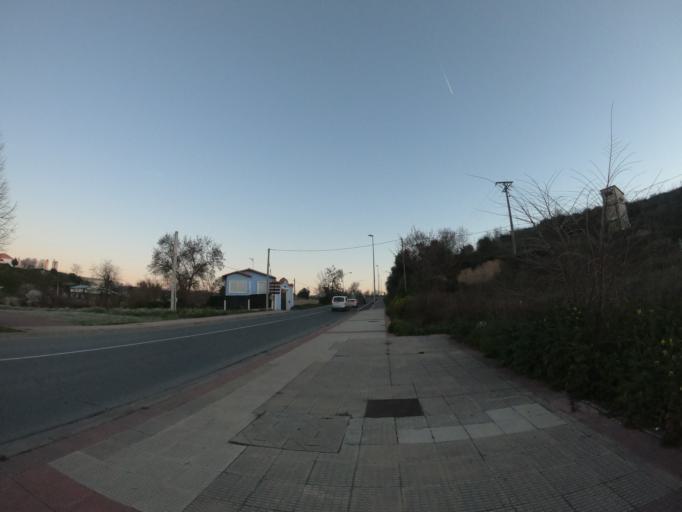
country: ES
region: La Rioja
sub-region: Provincia de La Rioja
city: Logrono
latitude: 42.4763
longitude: -2.4444
